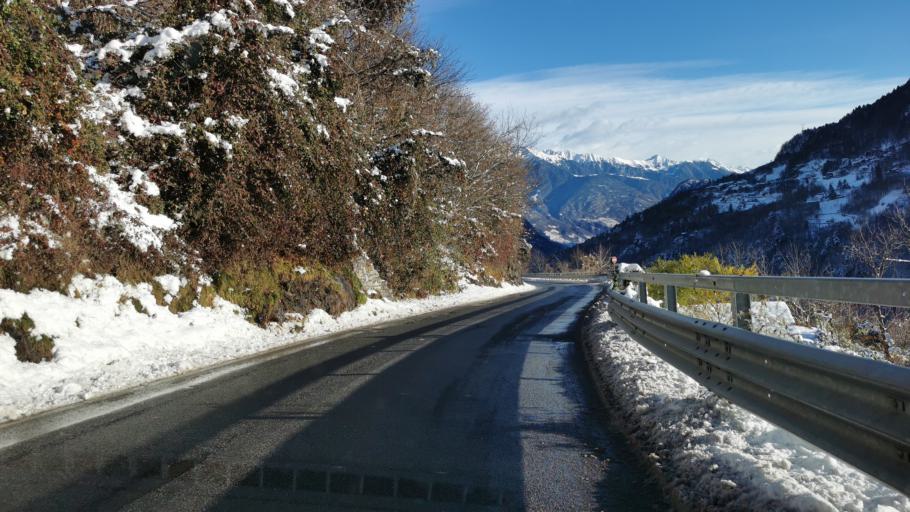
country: IT
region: Lombardy
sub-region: Provincia di Sondrio
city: Bema
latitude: 46.1167
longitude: 9.5581
